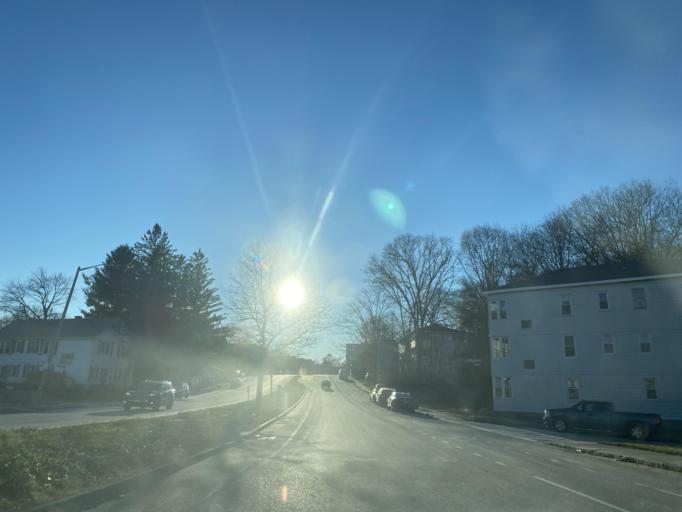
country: US
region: Massachusetts
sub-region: Worcester County
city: Hamilton
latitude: 42.2593
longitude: -71.7651
